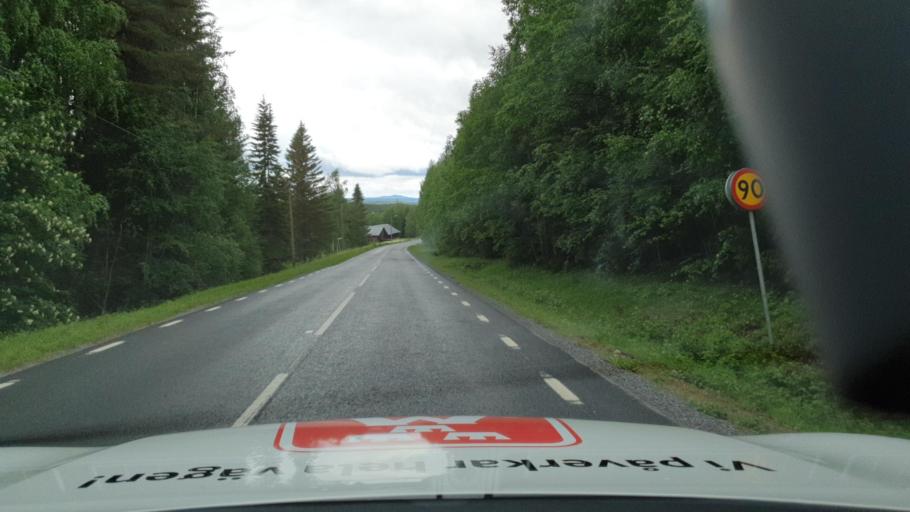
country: SE
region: Vaesterbotten
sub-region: Dorotea Kommun
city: Dorotea
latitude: 64.2390
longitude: 16.5398
